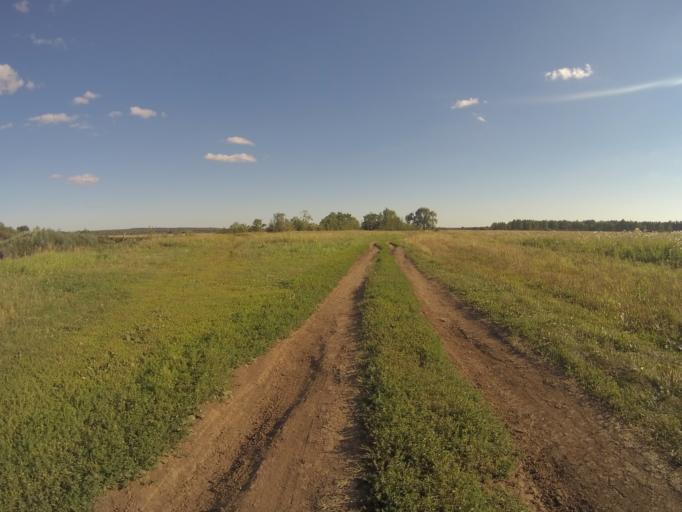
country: RU
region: Vladimir
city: Vladimir
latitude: 56.0990
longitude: 40.4002
